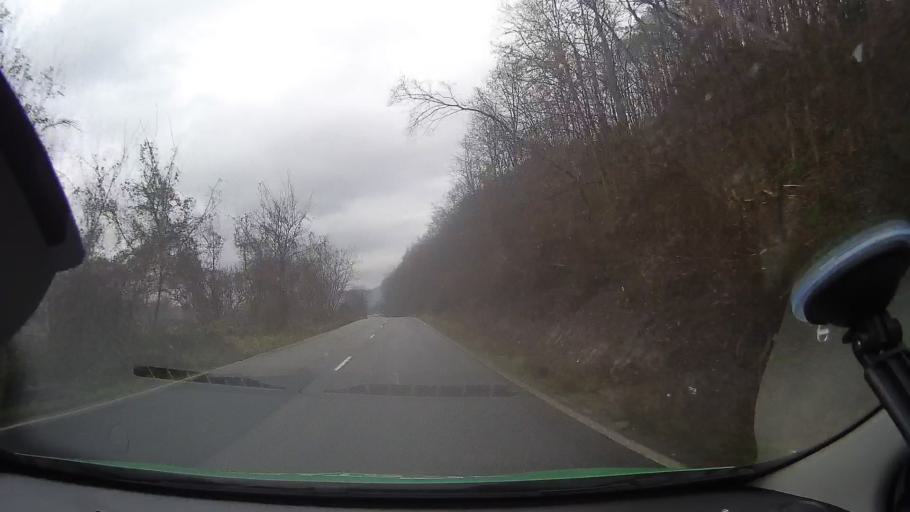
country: RO
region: Arad
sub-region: Comuna Buteni
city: Buteni
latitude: 46.3050
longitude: 22.1547
